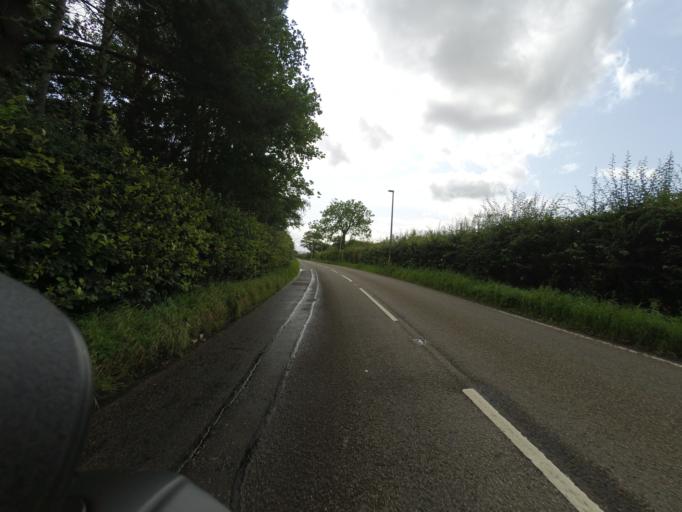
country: GB
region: Scotland
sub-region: Highland
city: Tain
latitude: 57.7410
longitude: -4.0789
